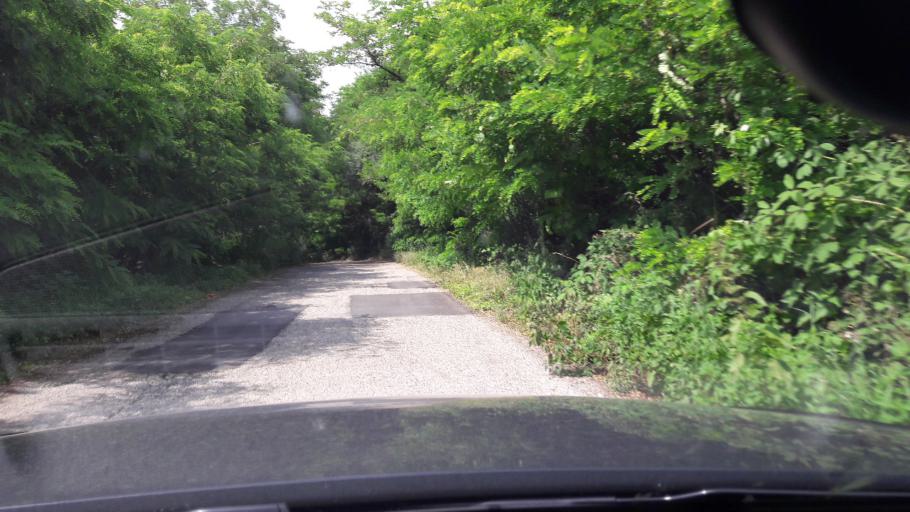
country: RS
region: Central Serbia
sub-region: Belgrade
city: Sopot
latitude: 44.6107
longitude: 20.5961
